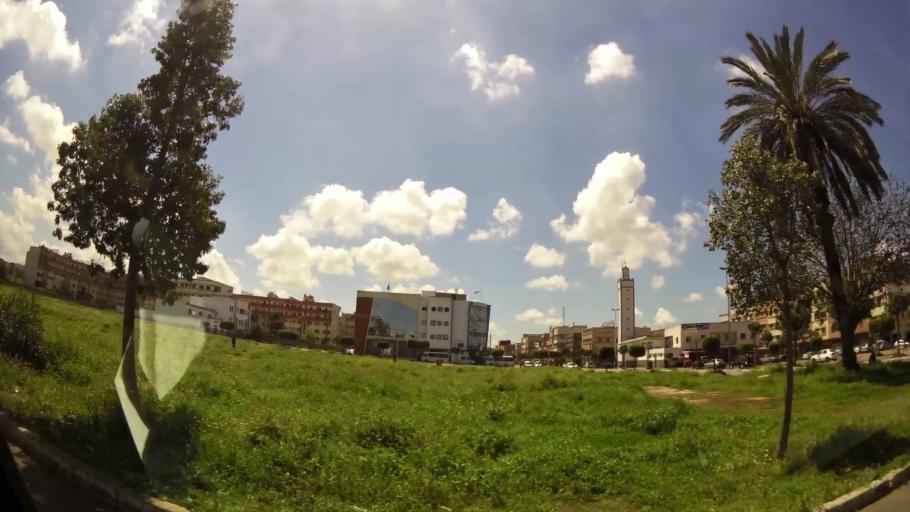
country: MA
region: Grand Casablanca
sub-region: Casablanca
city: Casablanca
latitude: 33.5603
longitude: -7.5793
